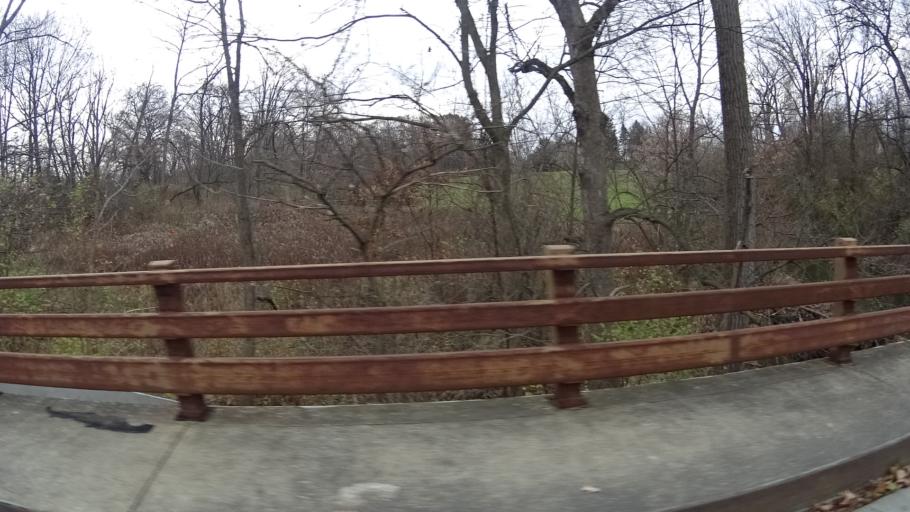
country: US
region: Ohio
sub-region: Cuyahoga County
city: Olmsted Falls
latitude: 41.3508
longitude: -81.9005
